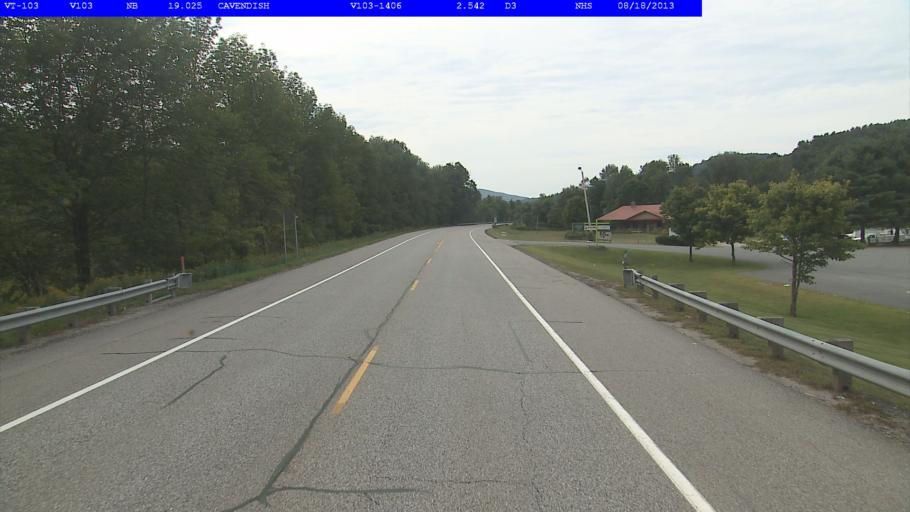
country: US
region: Vermont
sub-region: Windsor County
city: Chester
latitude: 43.3799
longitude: -72.6427
